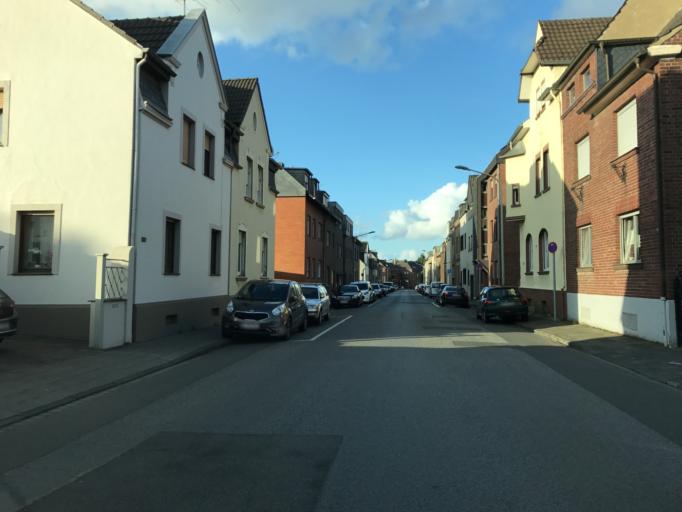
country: DE
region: North Rhine-Westphalia
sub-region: Regierungsbezirk Dusseldorf
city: Monchengladbach
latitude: 51.2203
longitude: 6.4424
